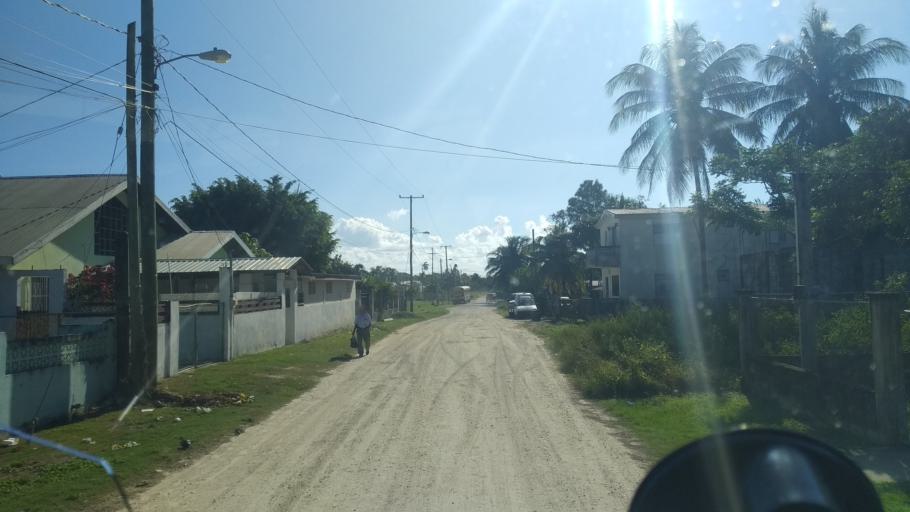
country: BZ
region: Belize
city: Belize City
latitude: 17.5510
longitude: -88.3255
